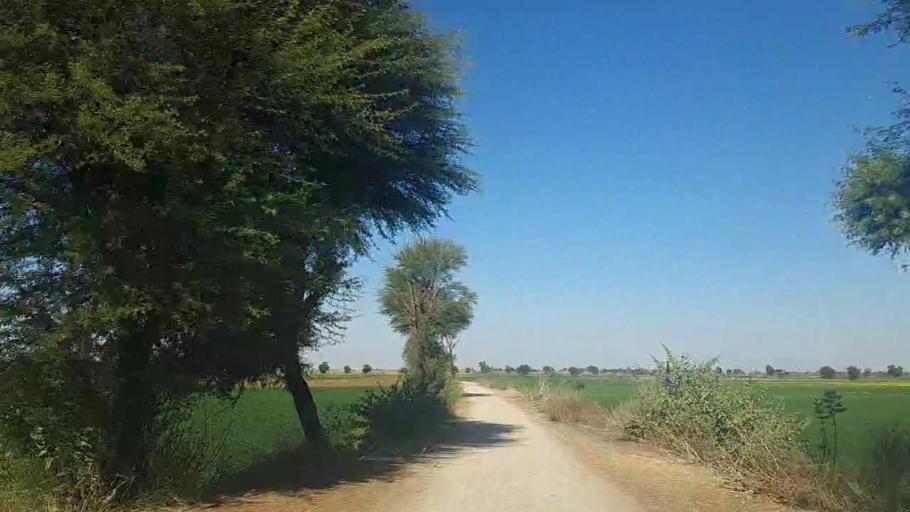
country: PK
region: Sindh
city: Khadro
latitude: 26.2193
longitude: 68.8591
